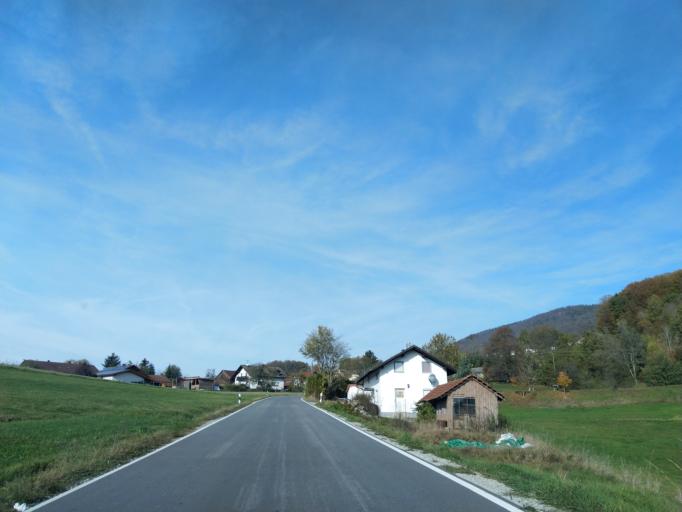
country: DE
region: Bavaria
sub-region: Lower Bavaria
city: Grattersdorf
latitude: 48.7903
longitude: 13.1844
